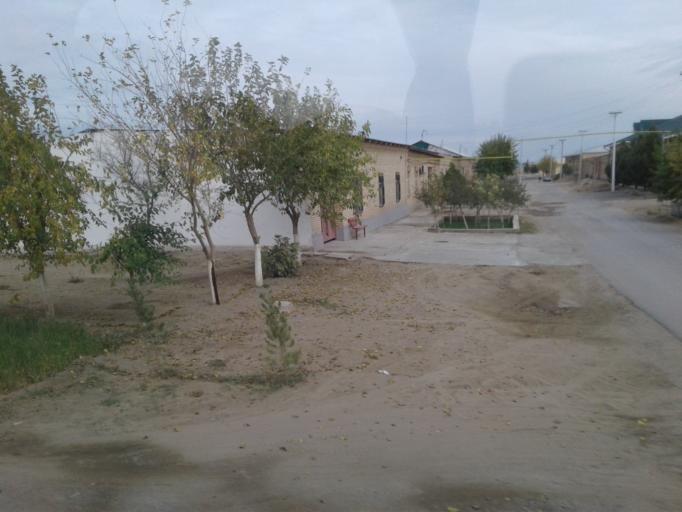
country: TM
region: Lebap
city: Turkmenabat
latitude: 38.9931
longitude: 63.5539
